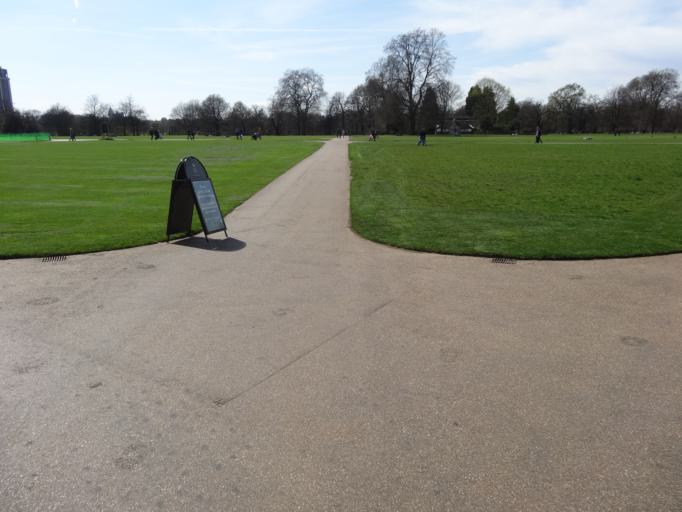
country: GB
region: England
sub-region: Greater London
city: Chelsea
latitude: 51.5082
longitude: -0.1583
